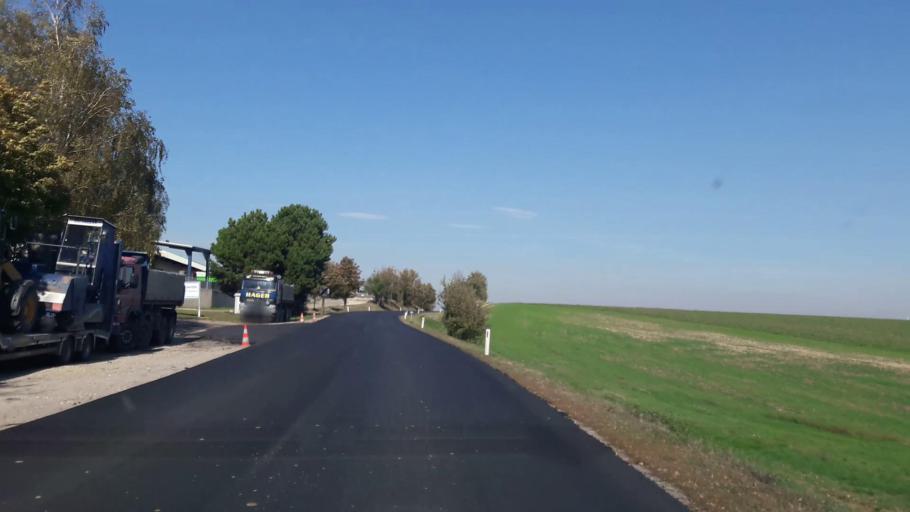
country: AT
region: Lower Austria
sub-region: Politischer Bezirk Korneuburg
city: Grossrussbach
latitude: 48.4642
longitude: 16.3778
